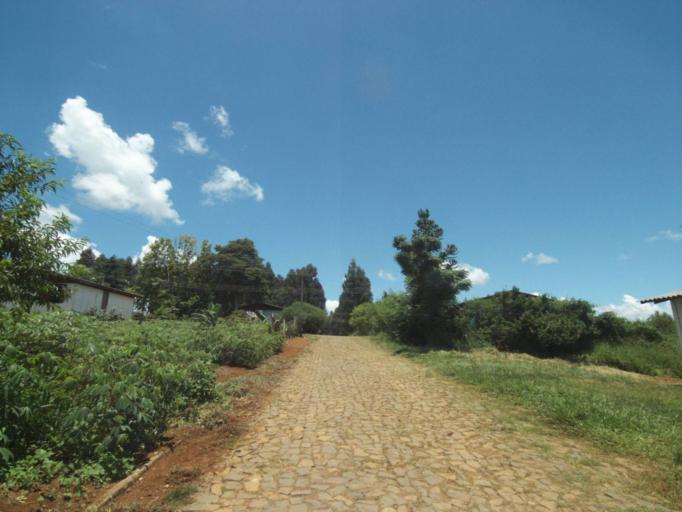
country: BR
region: Parana
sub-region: Pinhao
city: Pinhao
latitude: -25.7879
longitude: -52.0872
